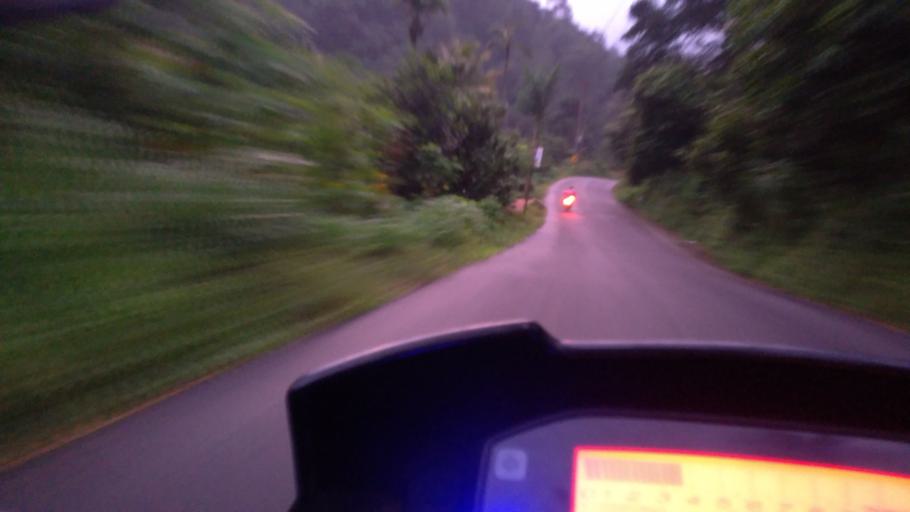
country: IN
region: Kerala
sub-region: Idukki
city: Munnar
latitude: 9.9659
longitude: 77.0648
